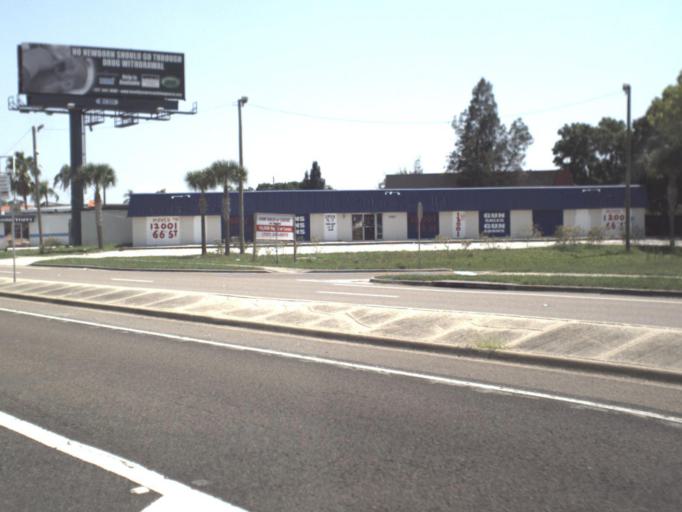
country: US
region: Florida
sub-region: Pinellas County
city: South Highpoint
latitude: 27.8901
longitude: -82.7200
